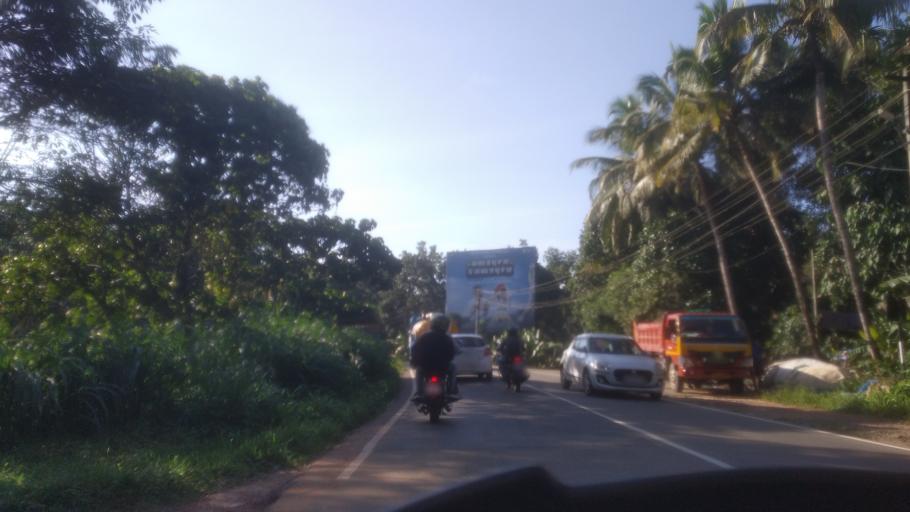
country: IN
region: Kerala
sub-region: Ernakulam
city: Ramamangalam
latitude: 9.9762
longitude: 76.5094
